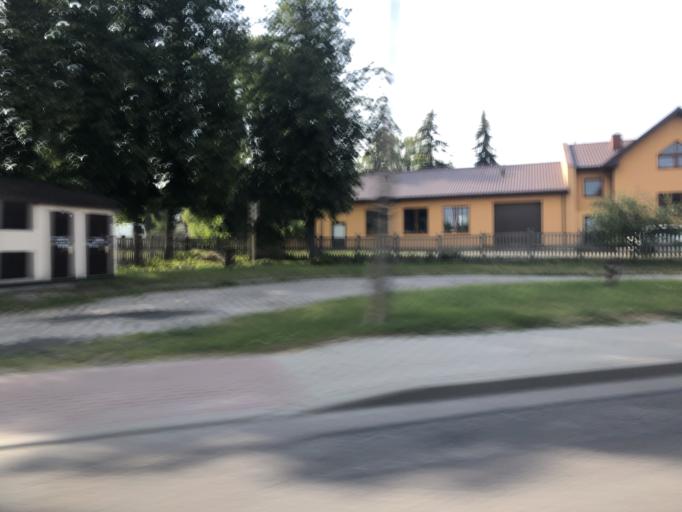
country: PL
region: Podlasie
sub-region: Lomza
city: Lomza
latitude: 53.1671
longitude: 22.0413
